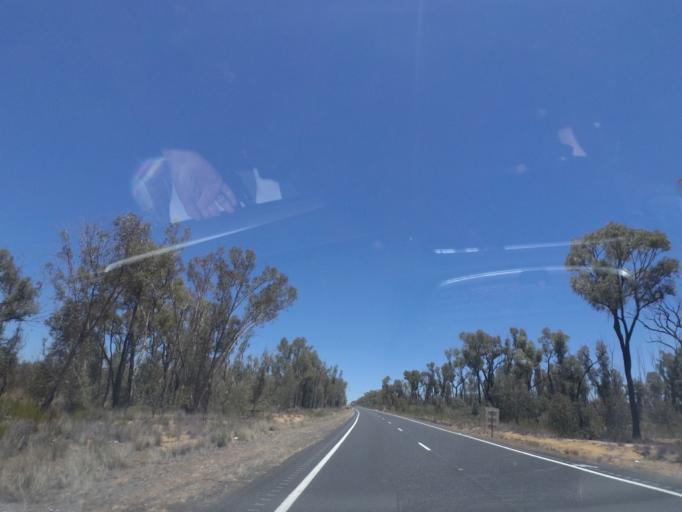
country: AU
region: New South Wales
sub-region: Warrumbungle Shire
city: Coonabarabran
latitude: -30.9456
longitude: 149.4223
